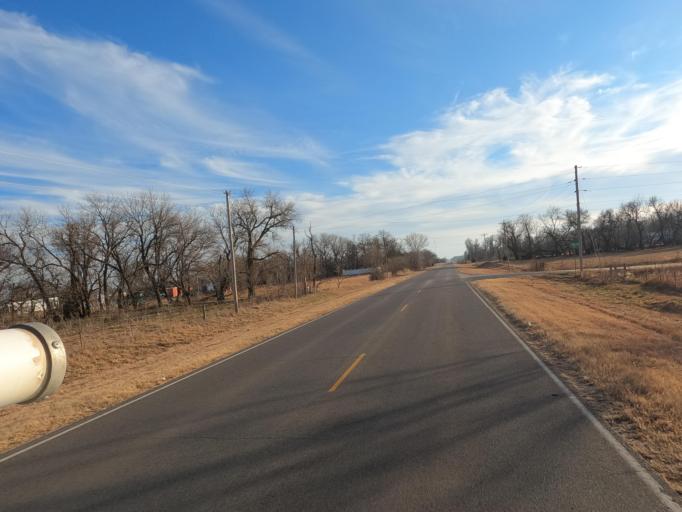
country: US
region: Kansas
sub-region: Reno County
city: Buhler
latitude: 38.1161
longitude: -97.7757
